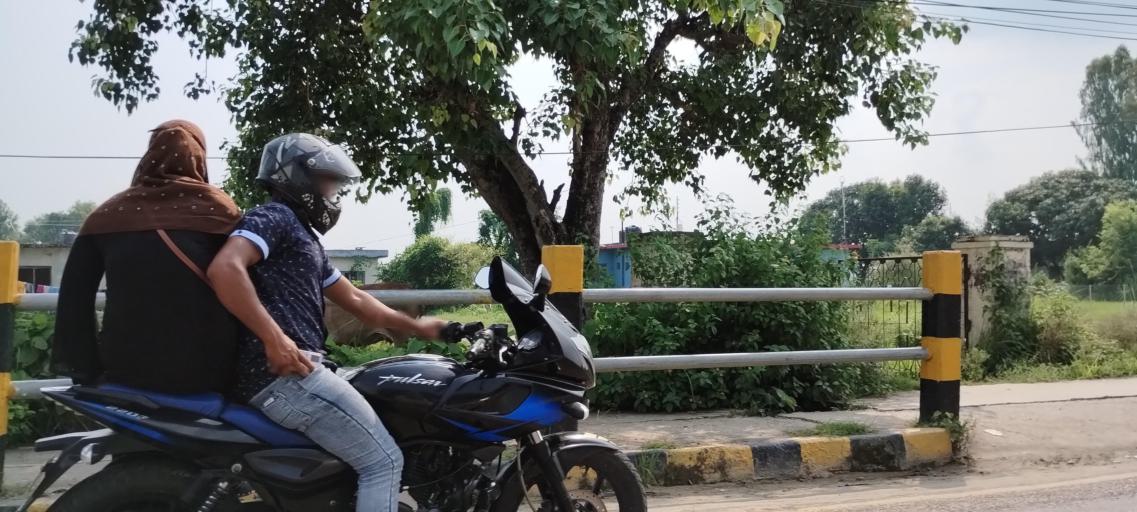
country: NP
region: Mid Western
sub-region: Bheri Zone
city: Nepalgunj
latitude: 28.0985
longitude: 81.6603
